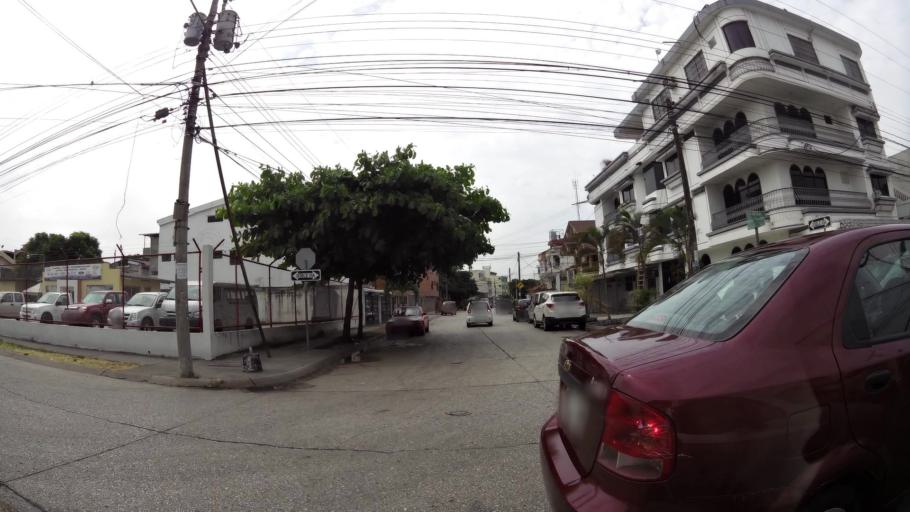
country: EC
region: Guayas
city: Eloy Alfaro
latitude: -2.1503
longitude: -79.8936
